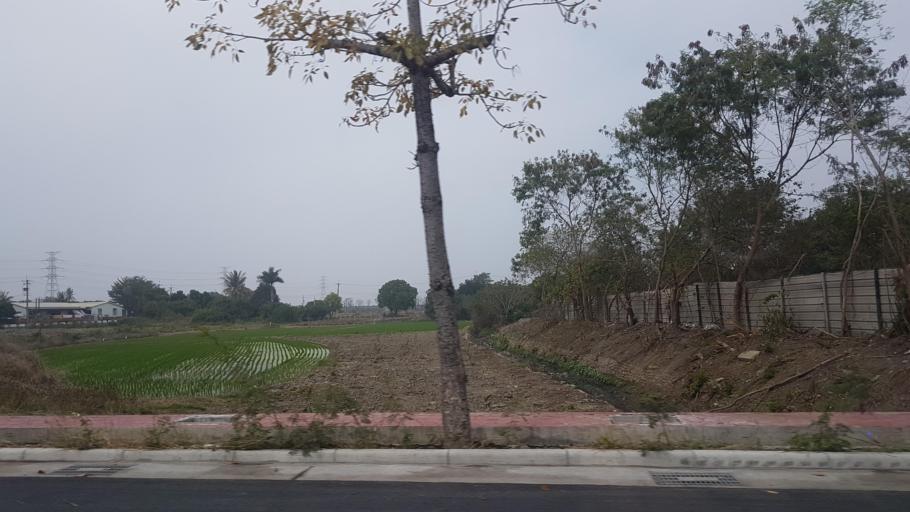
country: TW
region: Taiwan
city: Xinying
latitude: 23.3134
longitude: 120.2998
